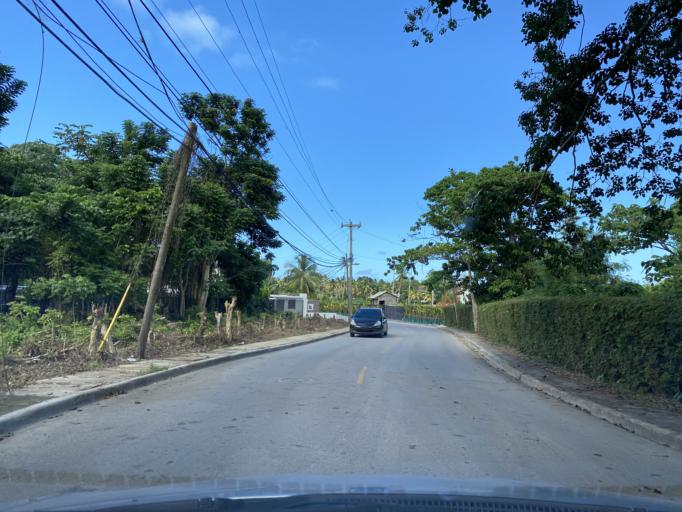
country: DO
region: Samana
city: Las Terrenas
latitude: 19.3076
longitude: -69.5634
